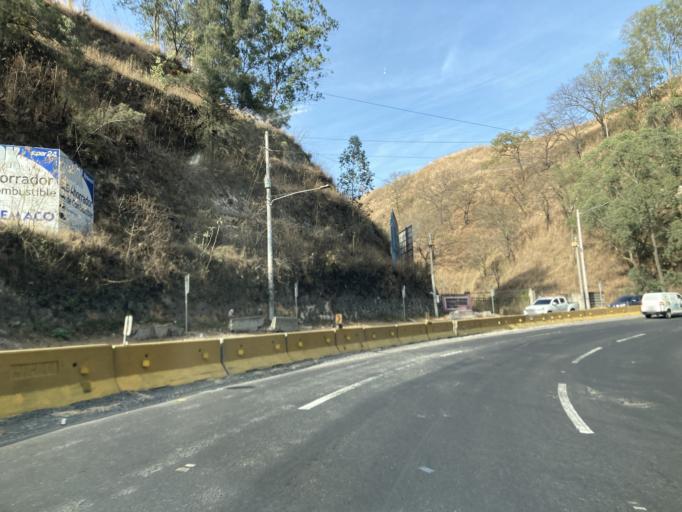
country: GT
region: Guatemala
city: Amatitlan
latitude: 14.5129
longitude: -90.6296
